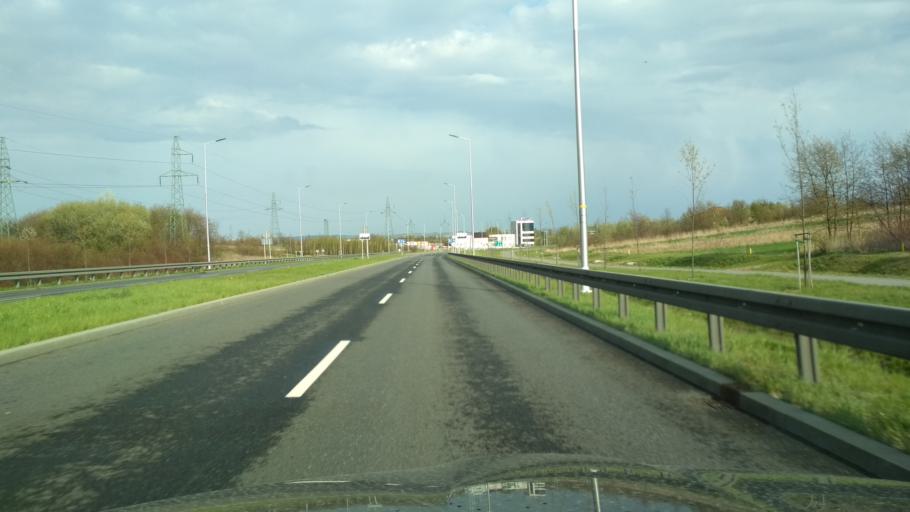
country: PL
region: Subcarpathian Voivodeship
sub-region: Powiat rzeszowski
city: Kielanowka
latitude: 50.0153
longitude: 21.9528
